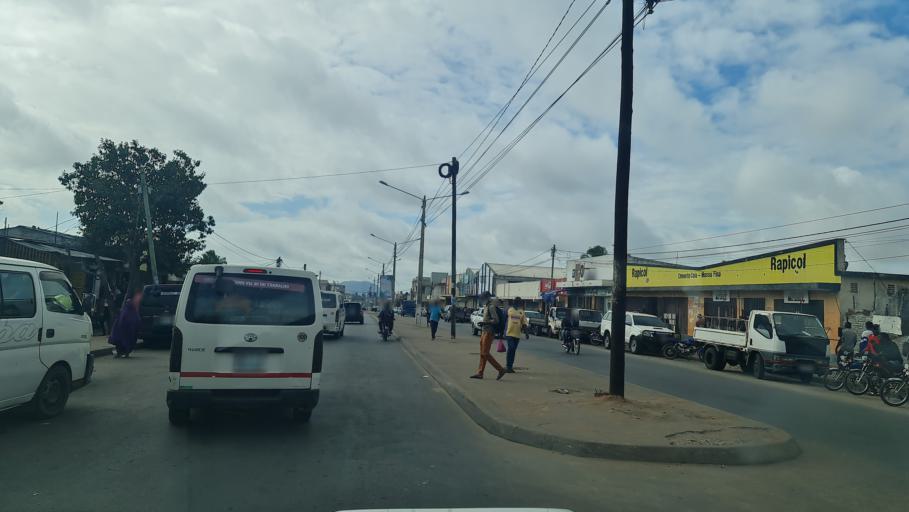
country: MZ
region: Nampula
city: Nampula
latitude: -15.1143
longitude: 39.2723
